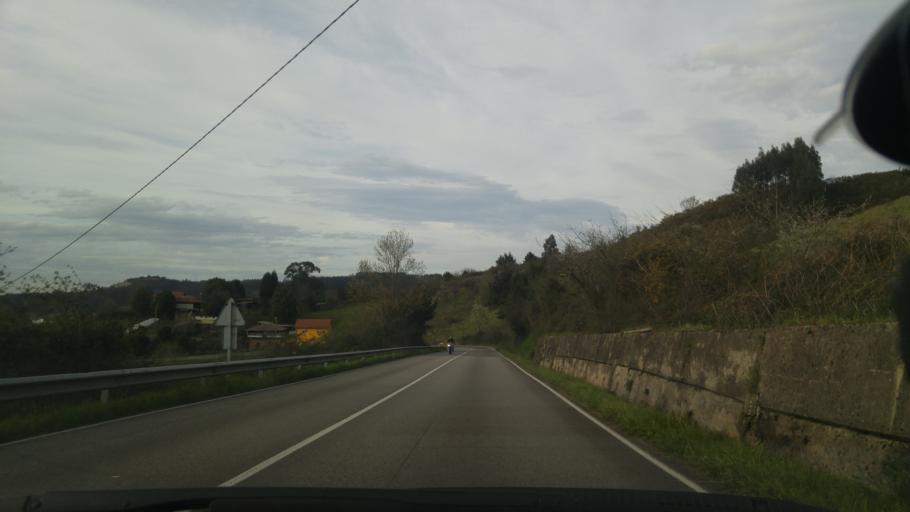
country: ES
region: Asturias
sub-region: Province of Asturias
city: Corvera de Asturias
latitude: 43.4797
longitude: -5.8482
